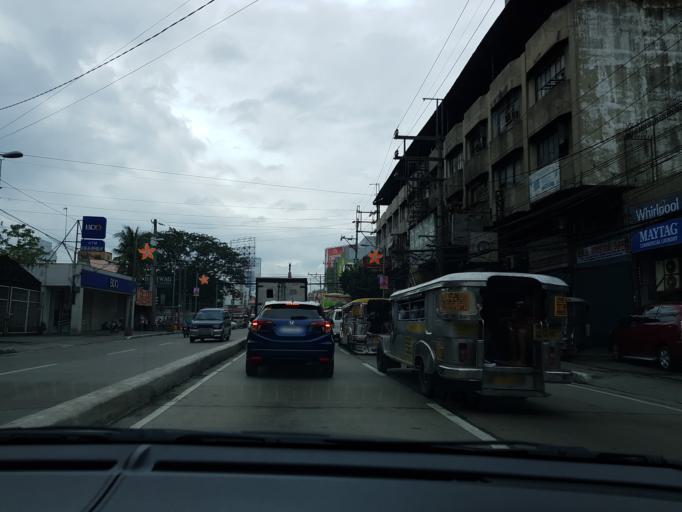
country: PH
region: Metro Manila
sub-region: Caloocan City
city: Niugan
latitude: 14.6593
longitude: 120.9840
